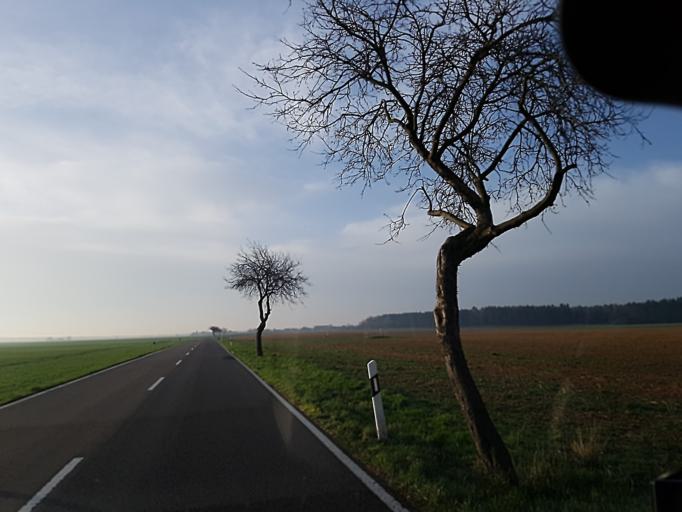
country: DE
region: Saxony
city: Strehla
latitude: 51.3899
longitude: 13.2746
